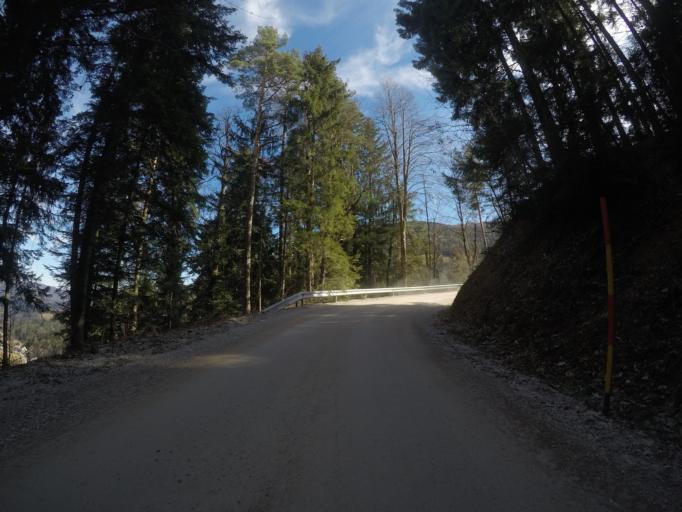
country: SI
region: Lovrenc na Pohorju
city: Lovrenc na Pohorju
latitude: 46.5279
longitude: 15.3768
